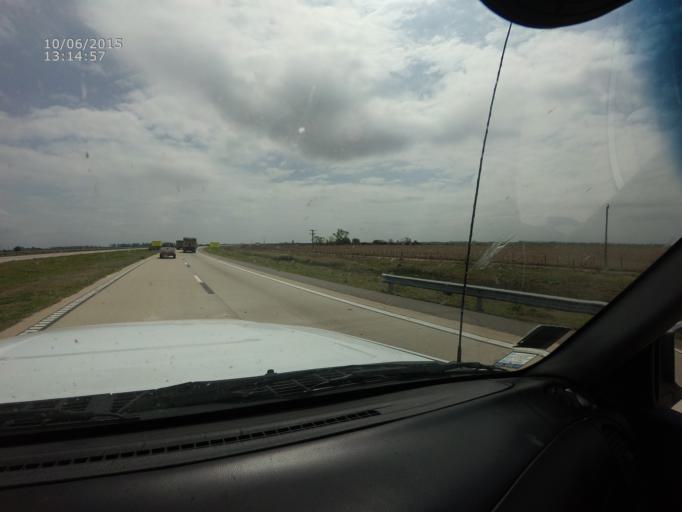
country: AR
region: Cordoba
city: General Roca
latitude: -32.7023
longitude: -61.9475
